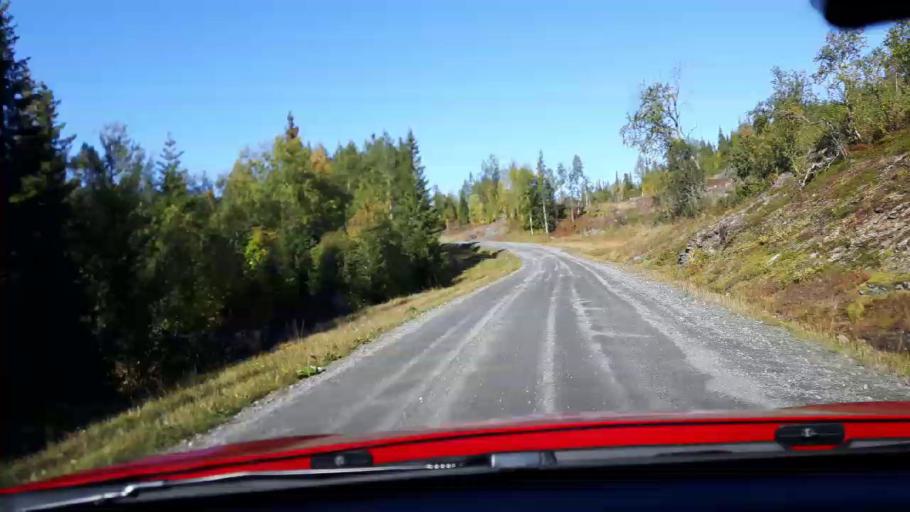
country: NO
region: Nord-Trondelag
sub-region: Lierne
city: Sandvika
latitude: 64.6077
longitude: 13.7102
